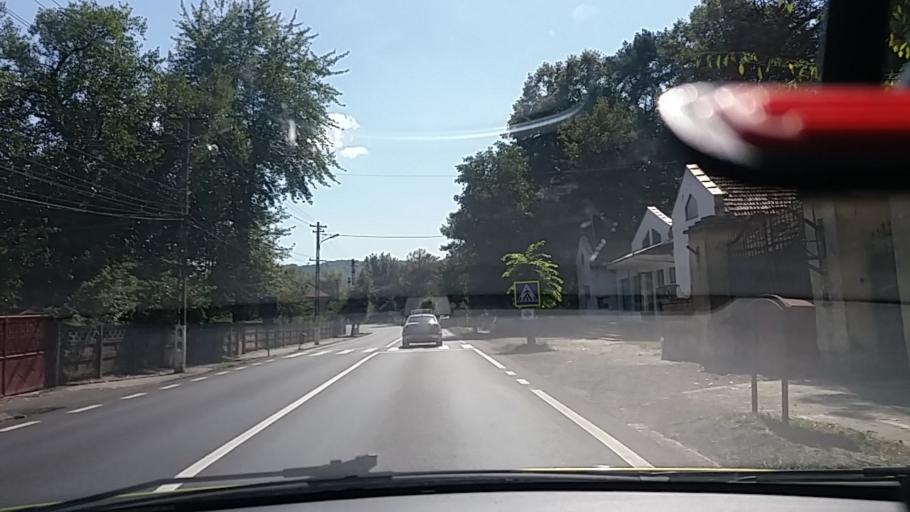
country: RO
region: Hunedoara
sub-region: Comuna Ilia
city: Ilia
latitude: 45.9352
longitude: 22.6517
